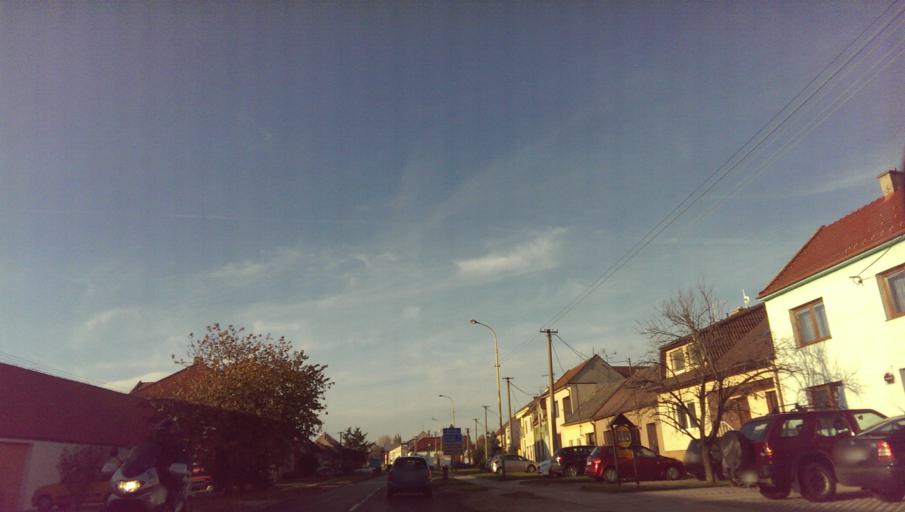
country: CZ
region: Zlin
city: Ostrozska Lhota
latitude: 48.9497
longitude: 17.4597
